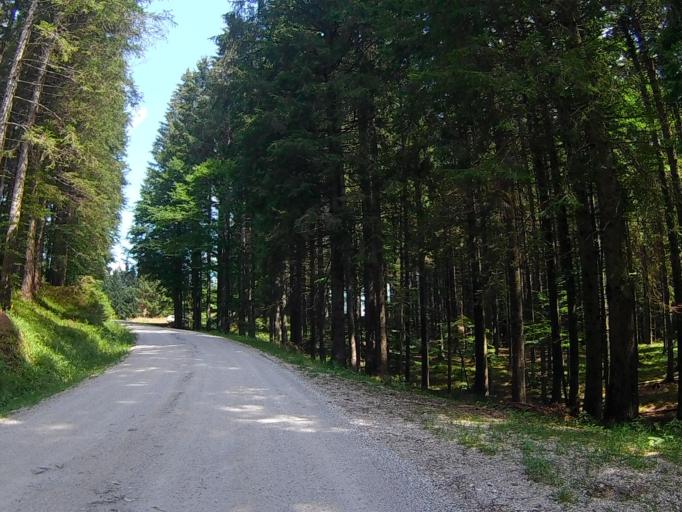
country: SI
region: Lovrenc na Pohorju
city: Lovrenc na Pohorju
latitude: 46.4822
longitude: 15.4450
